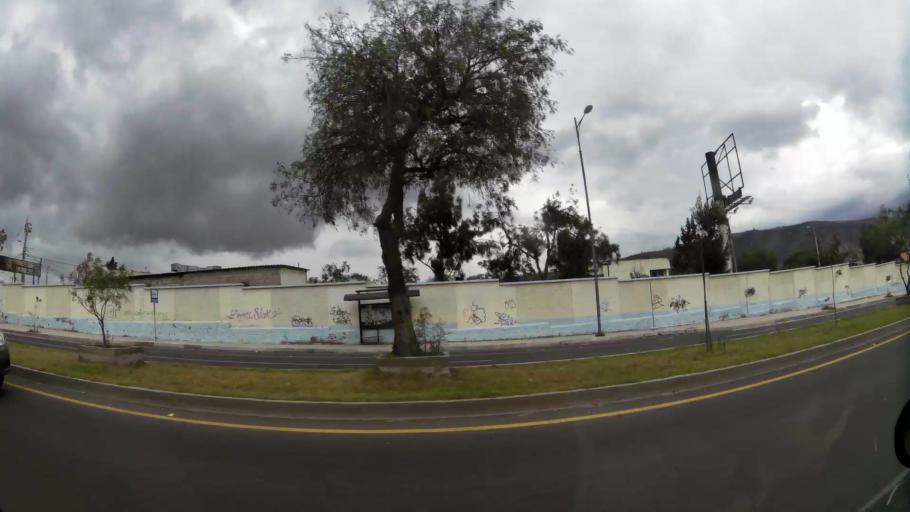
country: EC
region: Pichincha
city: Quito
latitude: -0.0081
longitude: -78.4531
